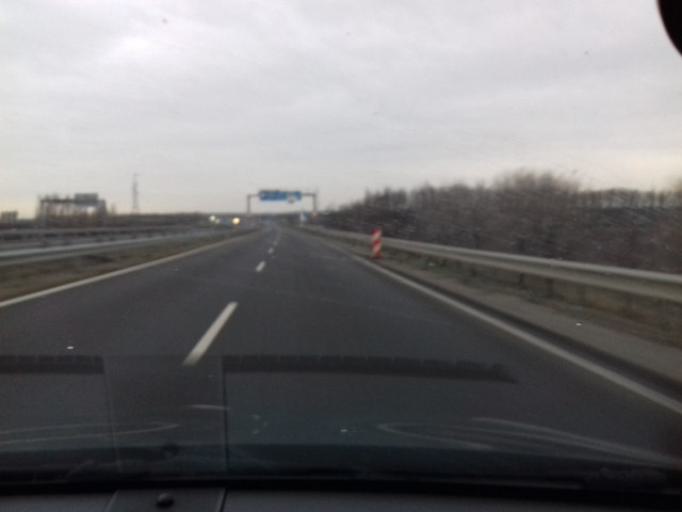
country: HU
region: Hajdu-Bihar
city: Debrecen
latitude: 47.5550
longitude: 21.5512
